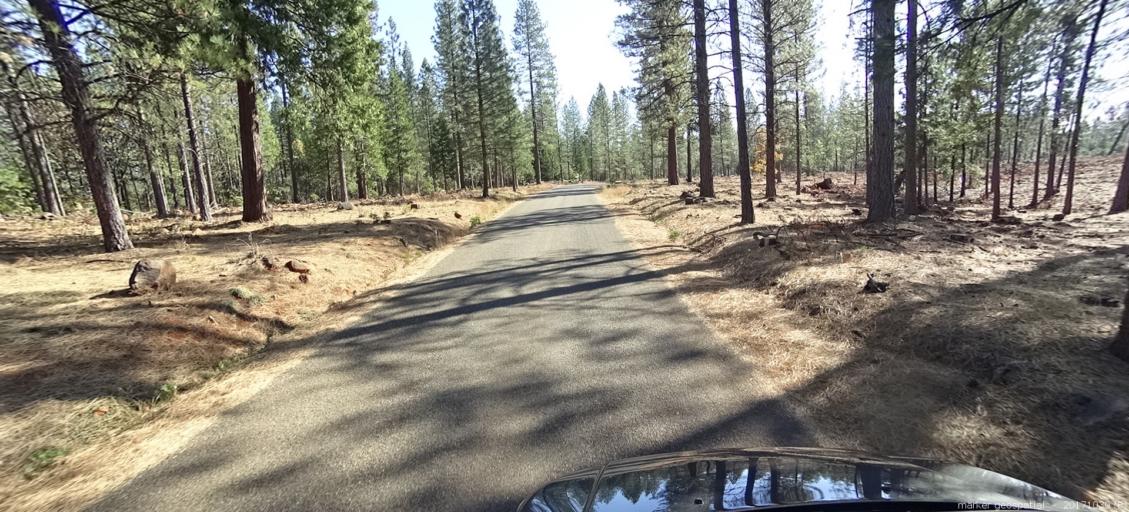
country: US
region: California
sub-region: Shasta County
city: Shingletown
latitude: 40.6144
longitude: -121.8814
